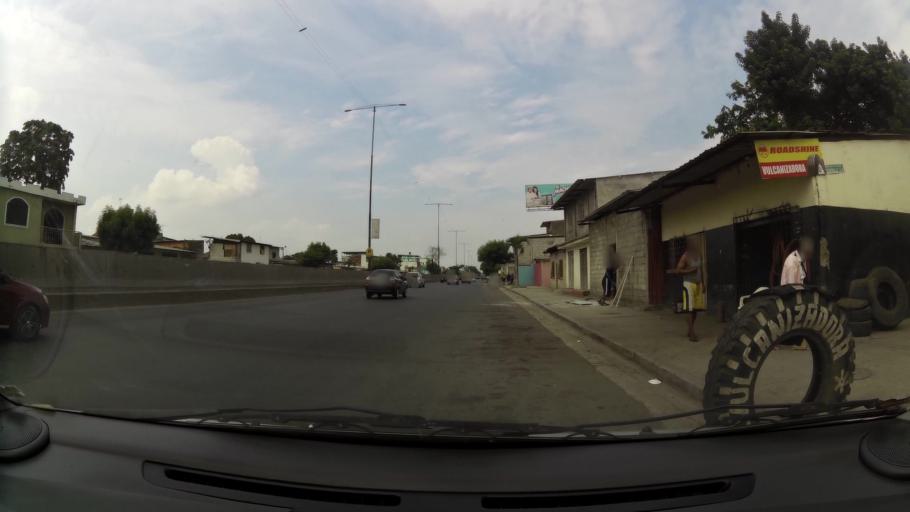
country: EC
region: Guayas
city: Guayaquil
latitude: -2.2390
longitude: -79.9097
